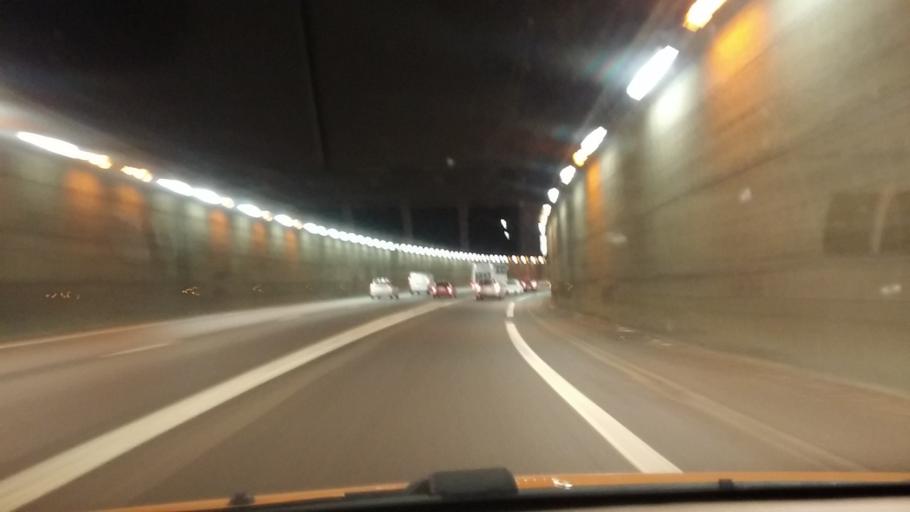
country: FR
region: Ile-de-France
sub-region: Departement du Val-de-Marne
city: Nogent-sur-Marne
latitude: 48.8389
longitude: 2.4935
